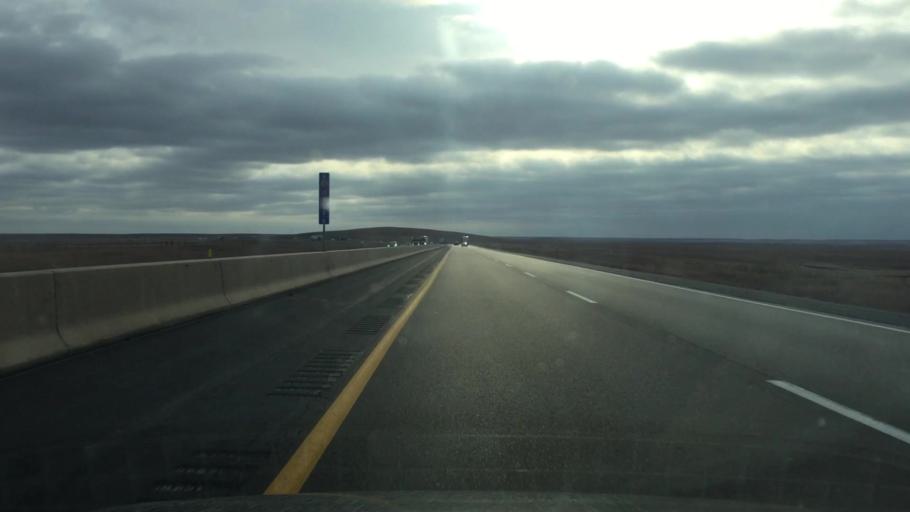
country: US
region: Kansas
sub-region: Chase County
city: Cottonwood Falls
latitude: 38.2230
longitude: -96.4295
